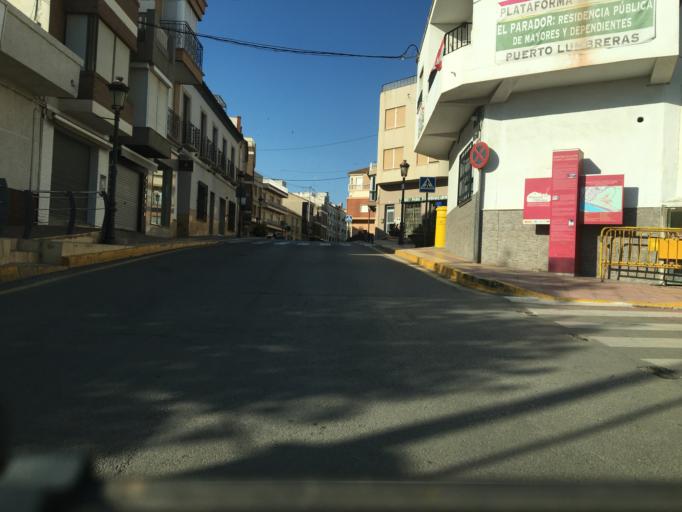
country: ES
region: Murcia
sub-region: Murcia
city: Puerto Lumbreras
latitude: 37.5603
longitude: -1.8101
